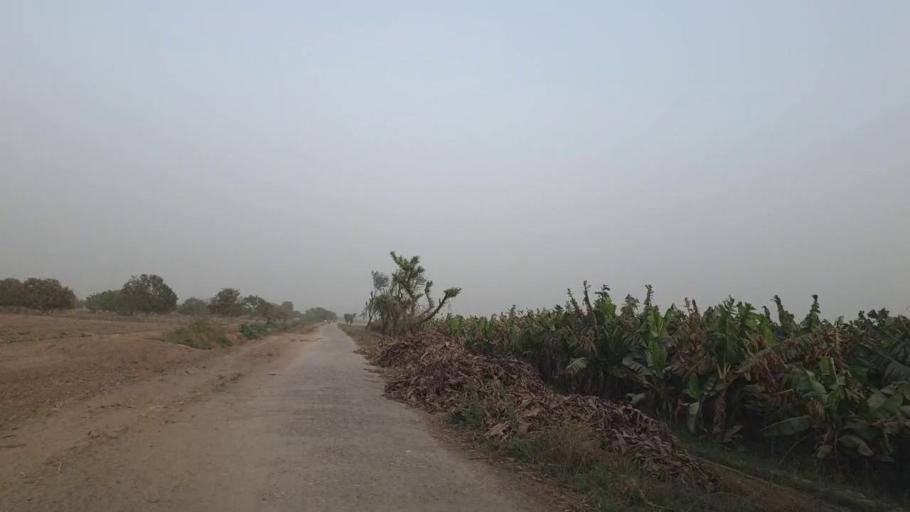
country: PK
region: Sindh
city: Kunri
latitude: 25.1194
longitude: 69.5396
